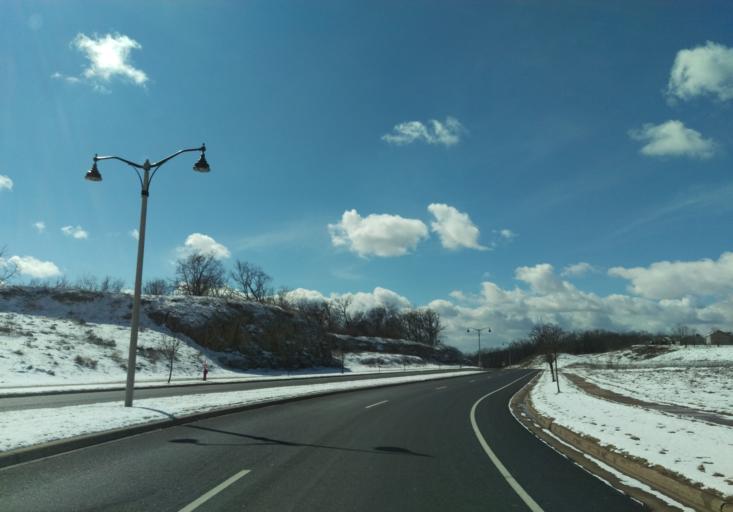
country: US
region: Wisconsin
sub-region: Dane County
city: Fitchburg
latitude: 43.0120
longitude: -89.4809
